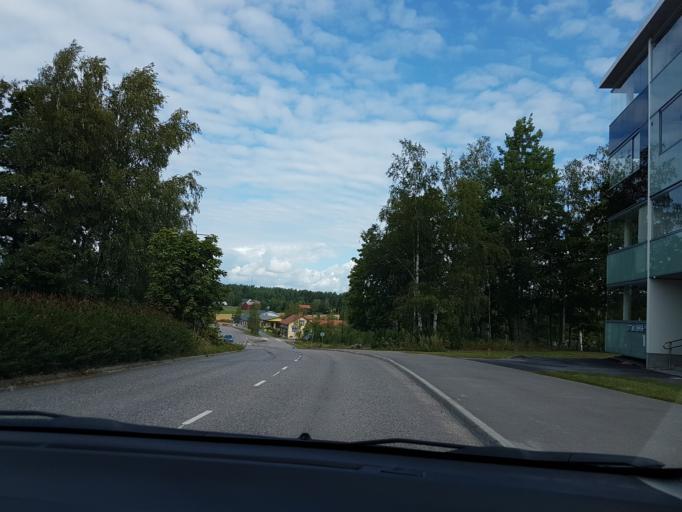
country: FI
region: Uusimaa
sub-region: Helsinki
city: Pornainen
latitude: 60.4781
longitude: 25.3744
